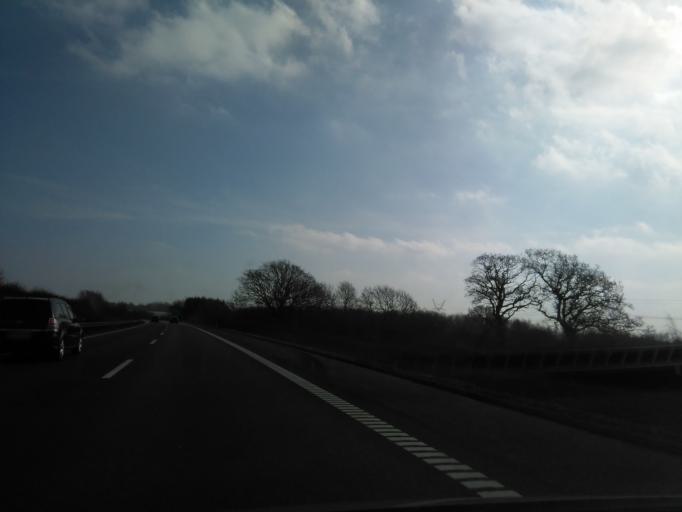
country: DK
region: South Denmark
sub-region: Fredericia Kommune
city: Taulov
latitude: 55.5413
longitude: 9.6549
